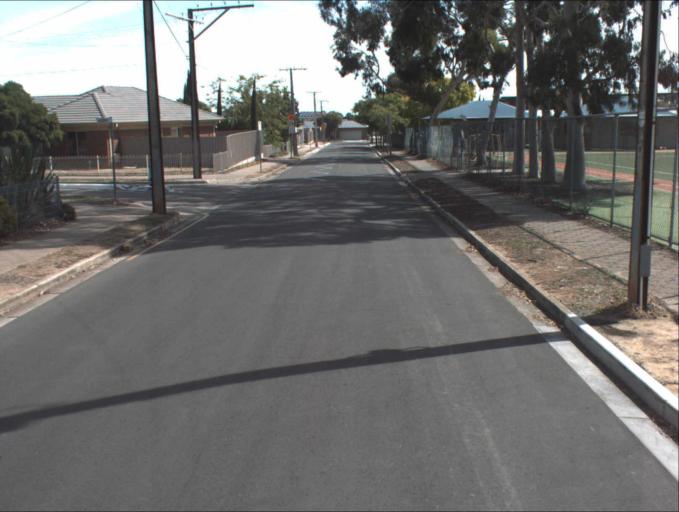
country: AU
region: South Australia
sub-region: Port Adelaide Enfield
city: Klemzig
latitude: -34.8684
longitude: 138.6440
